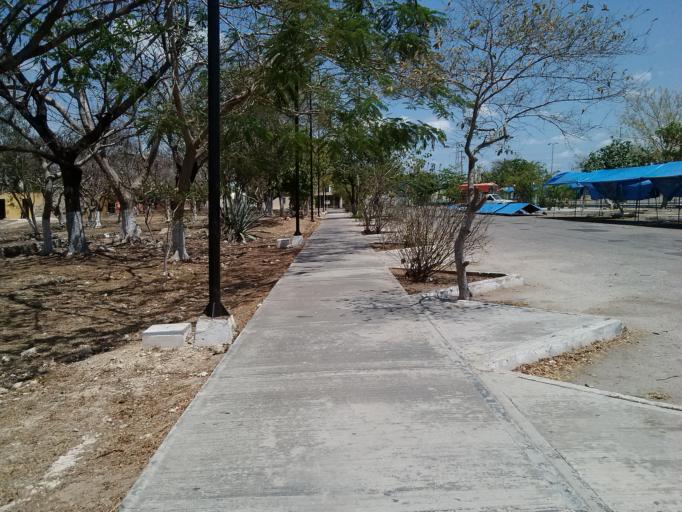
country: MX
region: Yucatan
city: Merida
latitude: 20.9690
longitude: -89.5832
